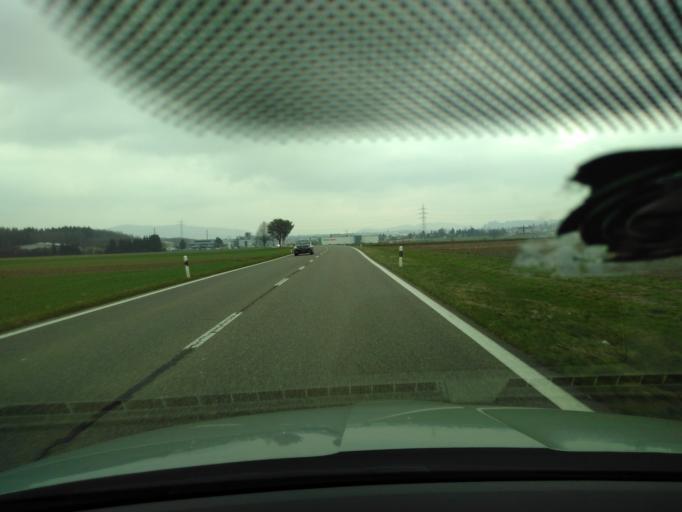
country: CH
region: Aargau
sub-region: Bezirk Aarau
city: Buchs
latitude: 47.3841
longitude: 8.1046
